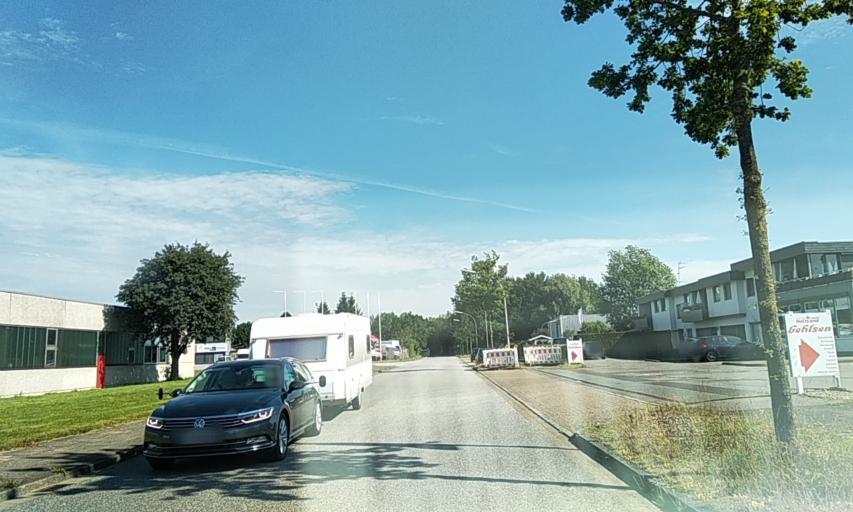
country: DE
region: Schleswig-Holstein
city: Fockbek
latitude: 54.3211
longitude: 9.6168
